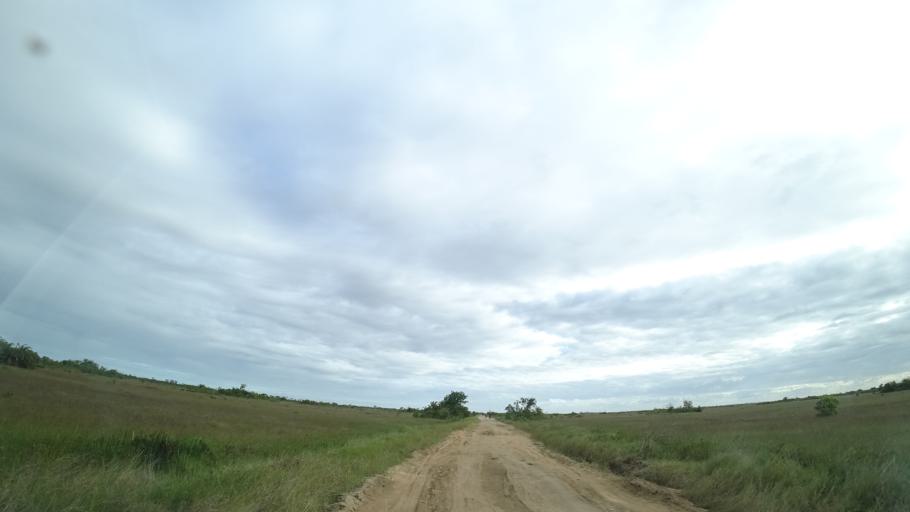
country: MZ
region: Sofala
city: Beira
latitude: -19.6983
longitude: 35.0300
